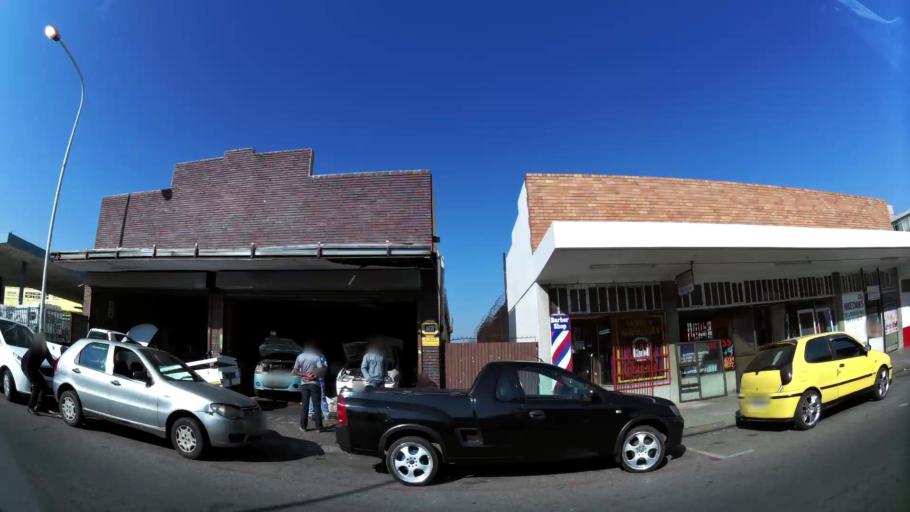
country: ZA
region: Gauteng
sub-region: Ekurhuleni Metropolitan Municipality
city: Boksburg
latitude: -26.2234
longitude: 28.2583
